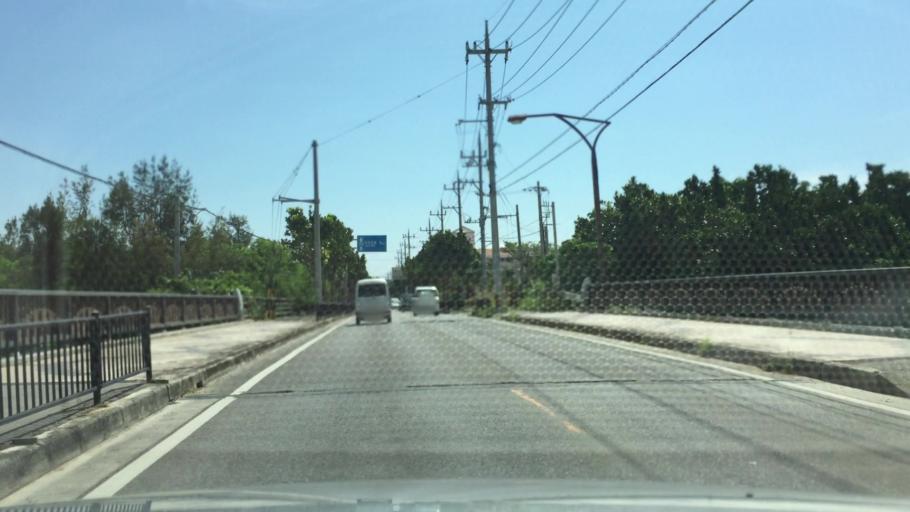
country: JP
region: Okinawa
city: Ishigaki
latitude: 24.3556
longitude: 124.2027
